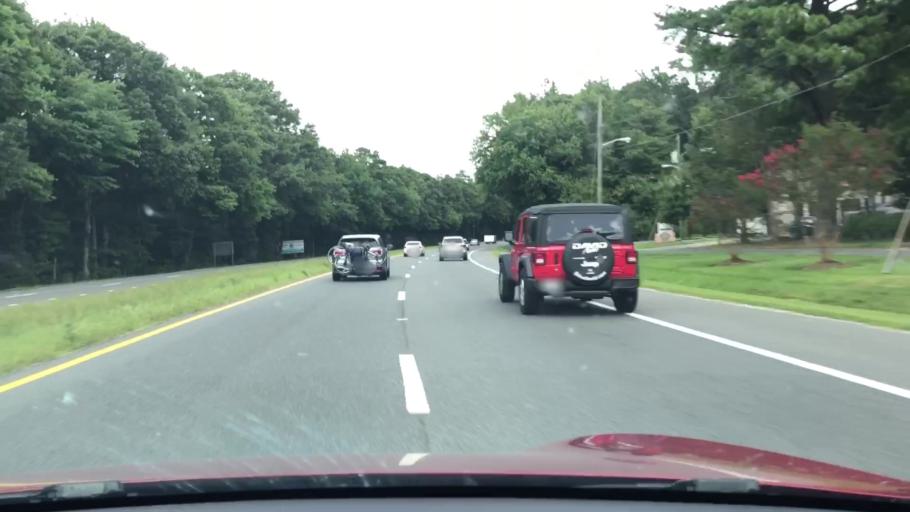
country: US
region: Virginia
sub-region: Northampton County
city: Exmore
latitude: 37.5356
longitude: -75.8288
